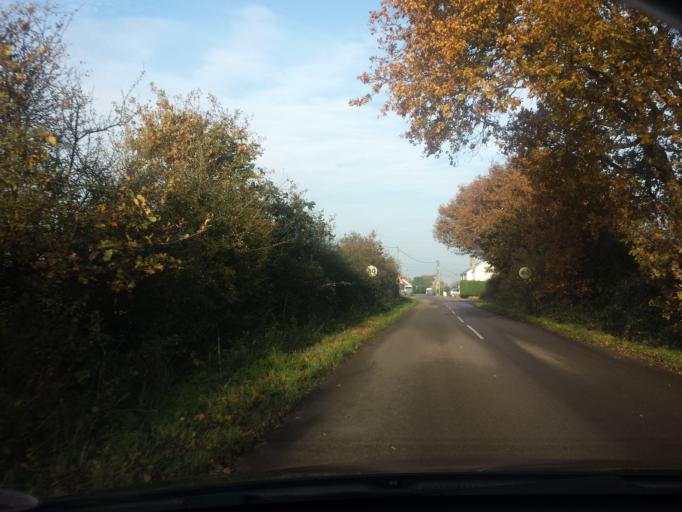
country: GB
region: England
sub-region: Essex
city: Little Clacton
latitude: 51.8416
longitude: 1.1232
